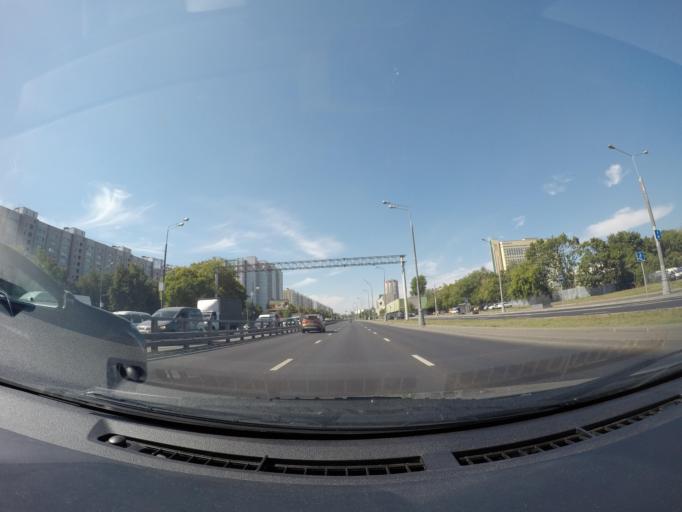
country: RU
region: Moscow
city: Vykhino-Zhulebino
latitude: 55.7115
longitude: 37.8190
